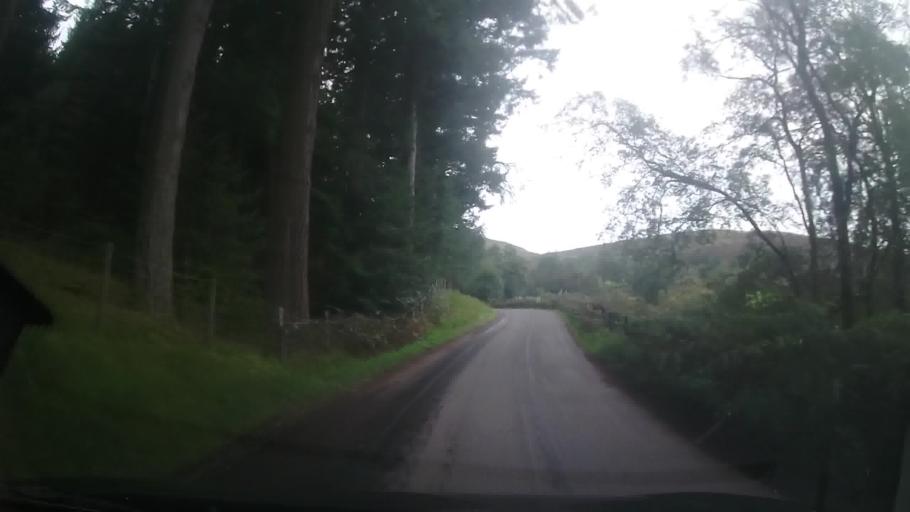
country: GB
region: Wales
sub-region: Sir Powys
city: Rhayader
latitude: 52.2923
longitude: -3.6092
